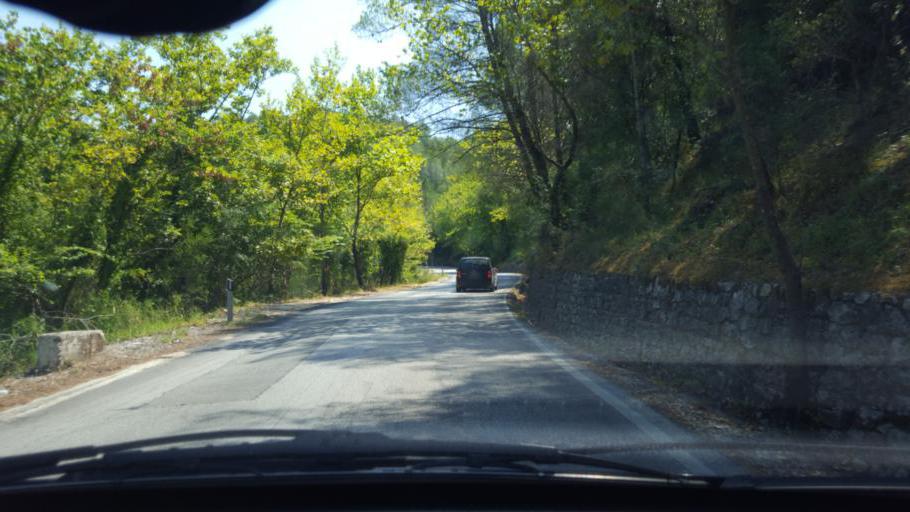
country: AL
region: Vlore
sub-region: Rrethi i Delvines
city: Mesopotam
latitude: 39.9210
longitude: 20.1575
